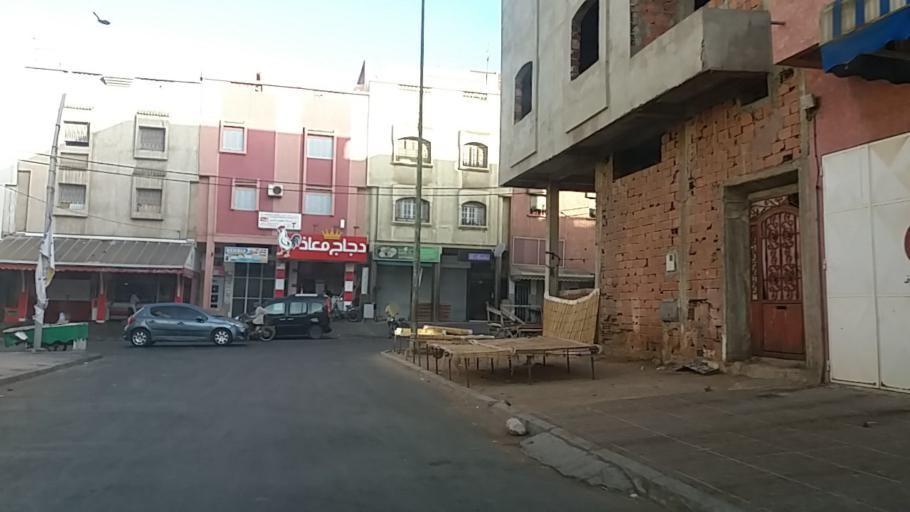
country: MA
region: Gharb-Chrarda-Beni Hssen
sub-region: Kenitra Province
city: Kenitra
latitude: 34.2560
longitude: -6.6224
